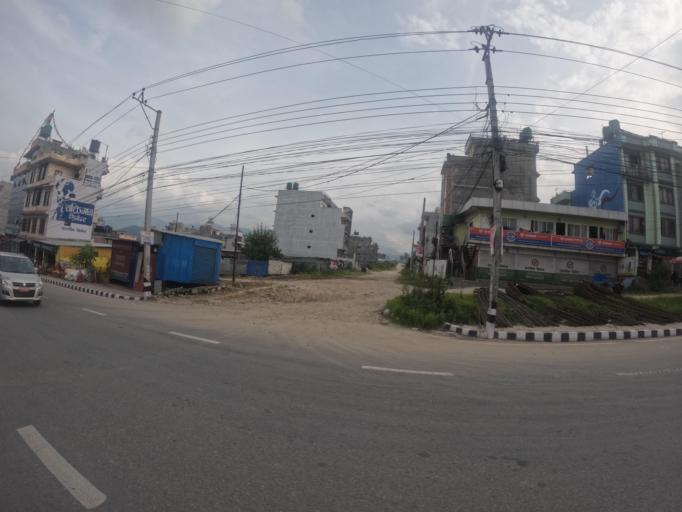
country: NP
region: Central Region
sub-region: Bagmati Zone
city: Bhaktapur
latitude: 27.6811
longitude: 85.3939
